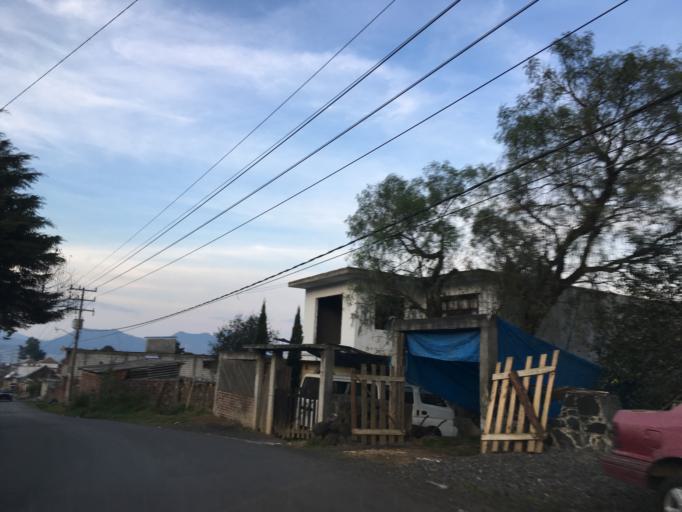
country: MX
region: Michoacan
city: Charapan
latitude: 19.6030
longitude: -102.2339
